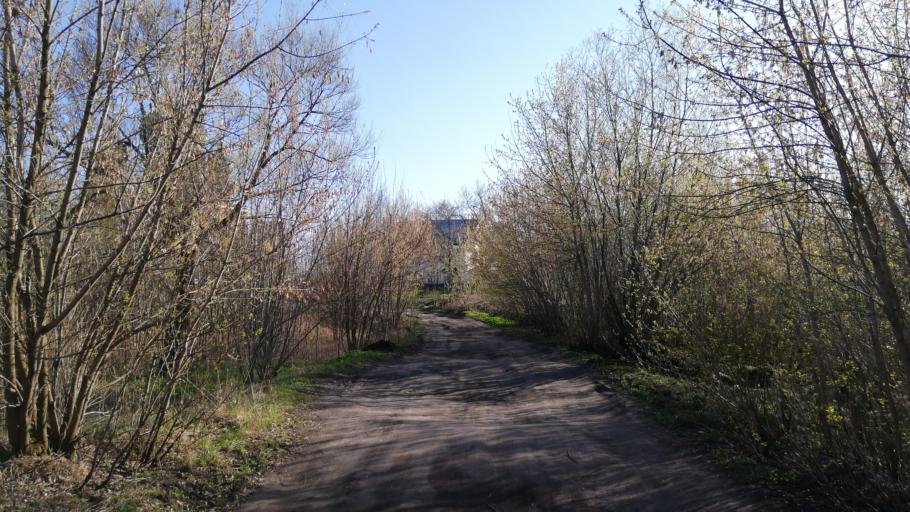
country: RU
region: Jaroslavl
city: Yaroslavl
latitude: 57.6127
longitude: 39.9063
